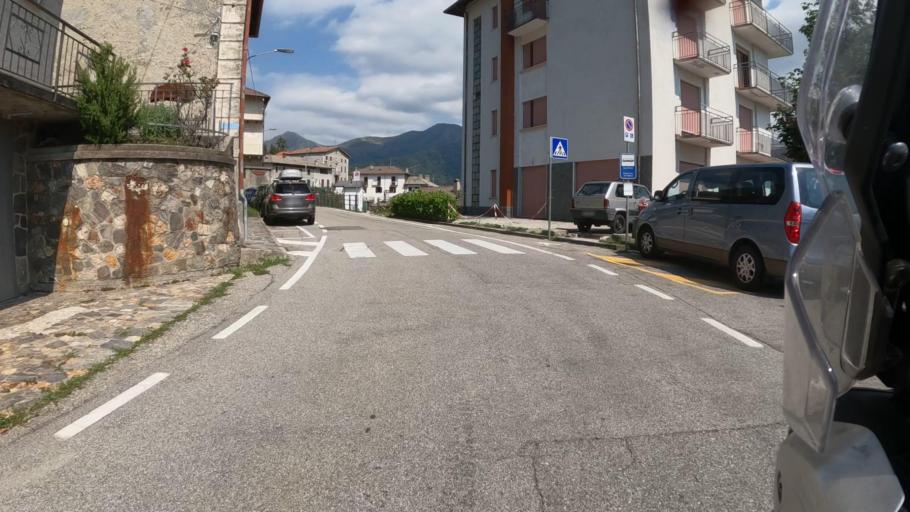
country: IT
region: Lombardy
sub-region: Provincia di Varese
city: Veddasca
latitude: 46.0707
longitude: 8.7979
